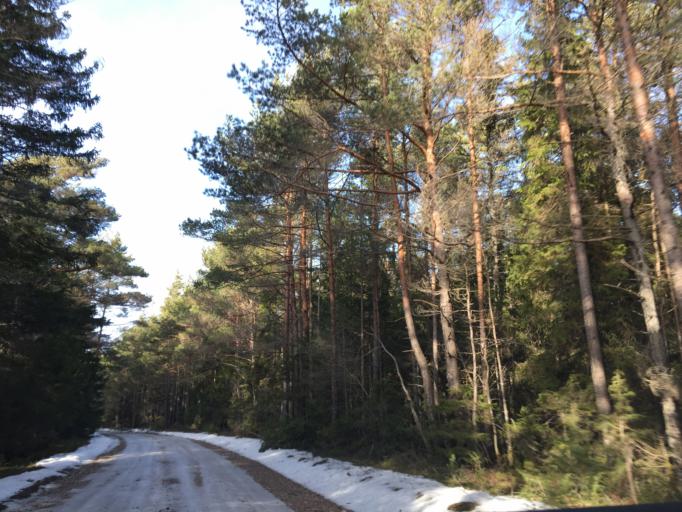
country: EE
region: Saare
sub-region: Kuressaare linn
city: Kuressaare
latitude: 58.4727
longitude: 21.9603
